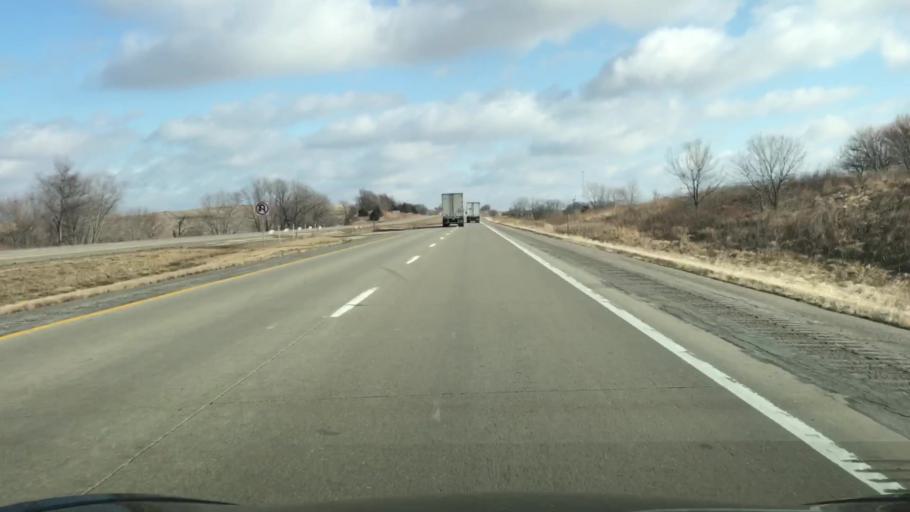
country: US
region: Iowa
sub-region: Cass County
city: Atlantic
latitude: 41.4972
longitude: -94.9910
